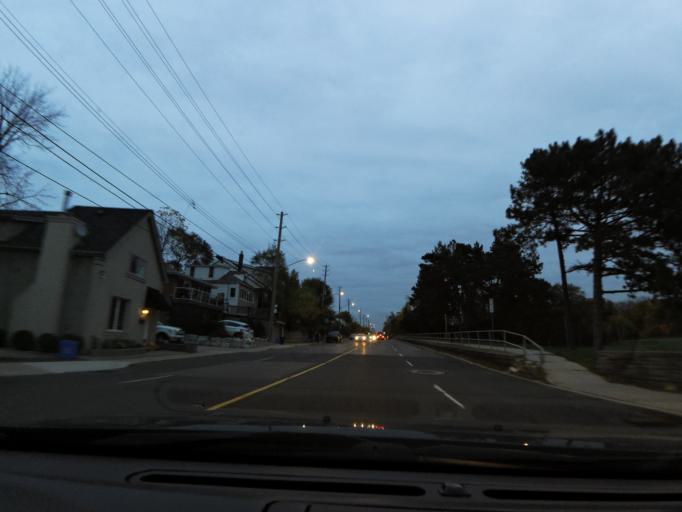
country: CA
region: Ontario
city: Hamilton
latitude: 43.2527
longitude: -79.8995
